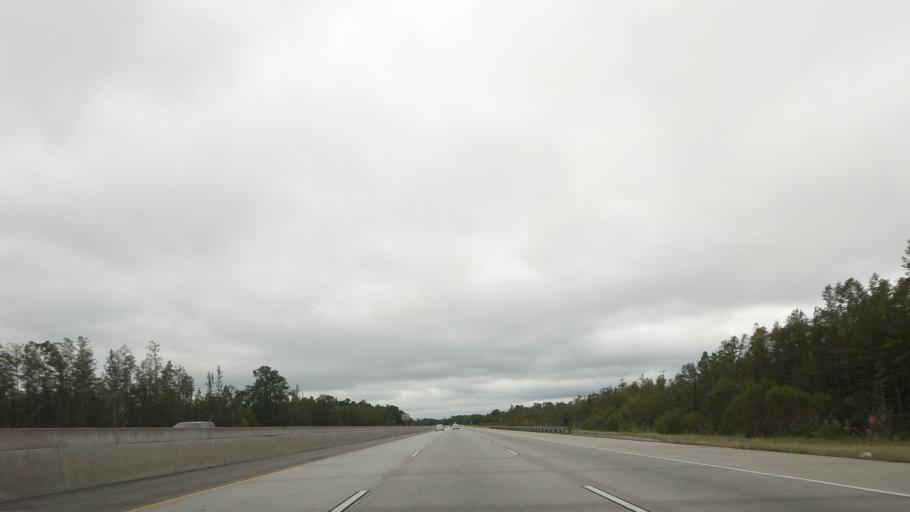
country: US
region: Georgia
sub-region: Lowndes County
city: Hahira
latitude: 31.0364
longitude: -83.3981
